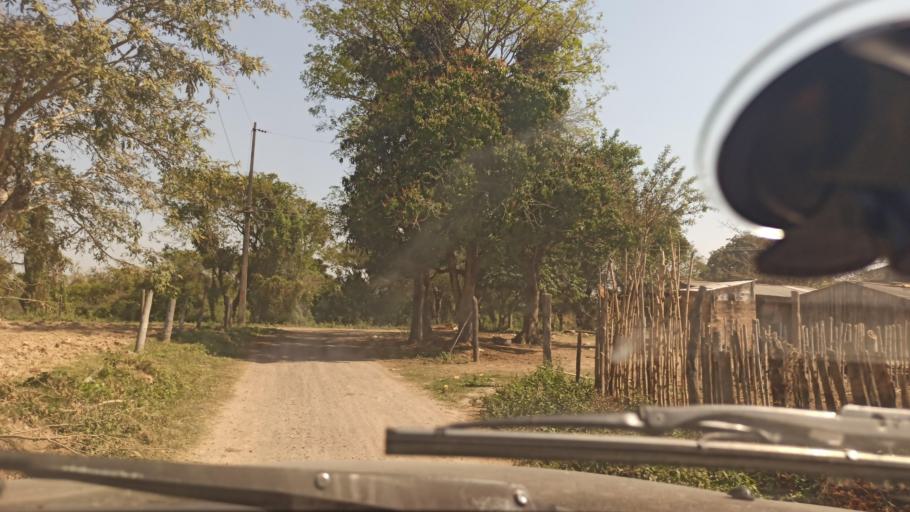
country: AR
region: Formosa
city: Clorinda
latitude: -25.3300
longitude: -57.6902
